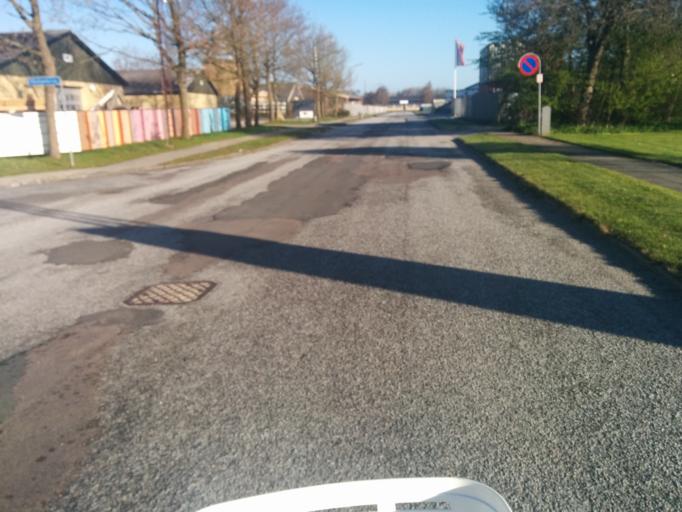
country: DK
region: Central Jutland
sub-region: Viborg Kommune
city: Viborg
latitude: 56.4640
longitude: 9.4010
